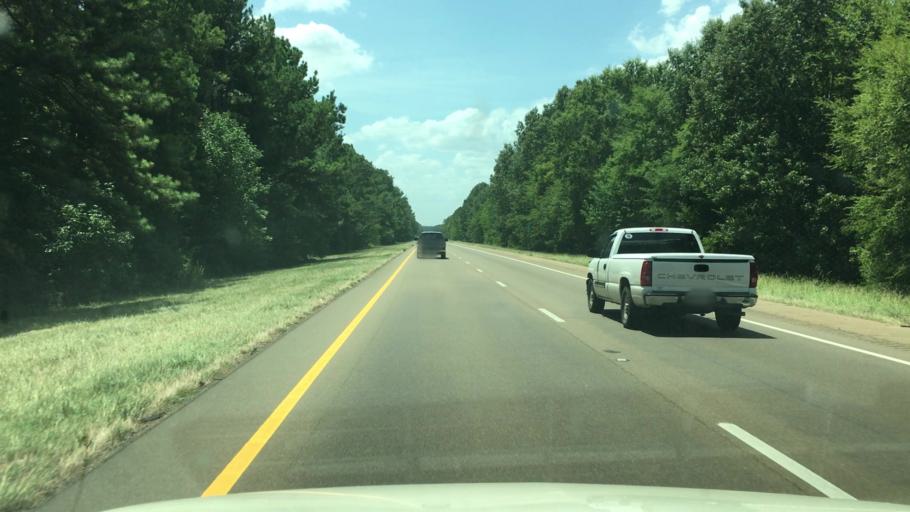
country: US
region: Texas
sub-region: Morris County
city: Naples
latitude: 33.3199
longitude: -94.6870
